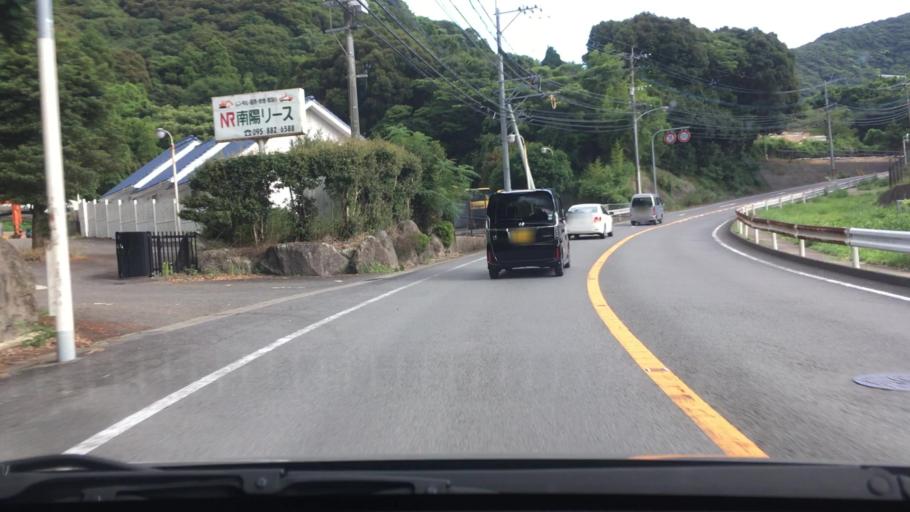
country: JP
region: Nagasaki
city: Togitsu
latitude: 32.8144
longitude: 129.8090
